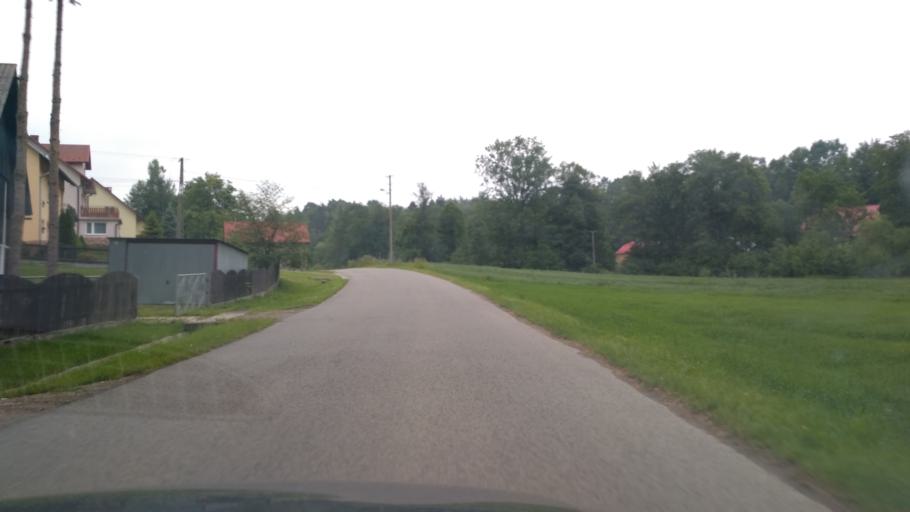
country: PL
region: Subcarpathian Voivodeship
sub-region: Powiat ropczycko-sedziszowski
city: Zagorzyce
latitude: 50.0130
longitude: 21.6769
